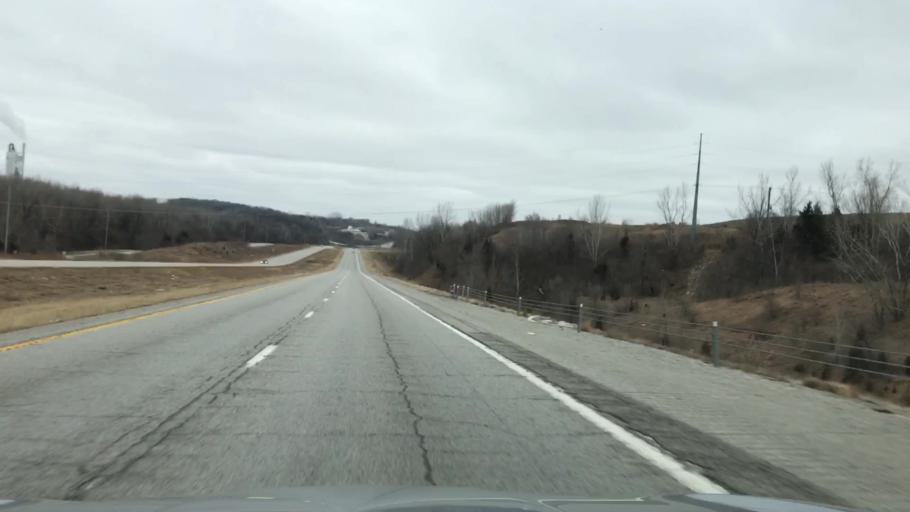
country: US
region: Missouri
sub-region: Jackson County
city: East Independence
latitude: 39.1344
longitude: -94.3843
